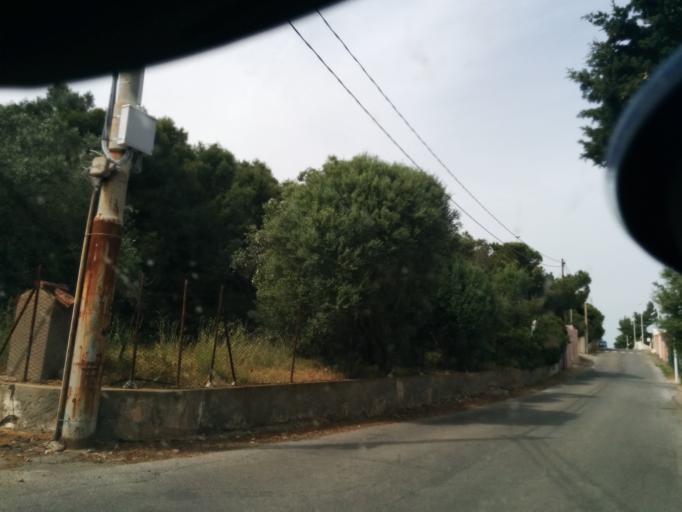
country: IT
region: Sardinia
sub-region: Provincia di Carbonia-Iglesias
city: Sant'Antioco
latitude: 38.9995
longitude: 8.4468
